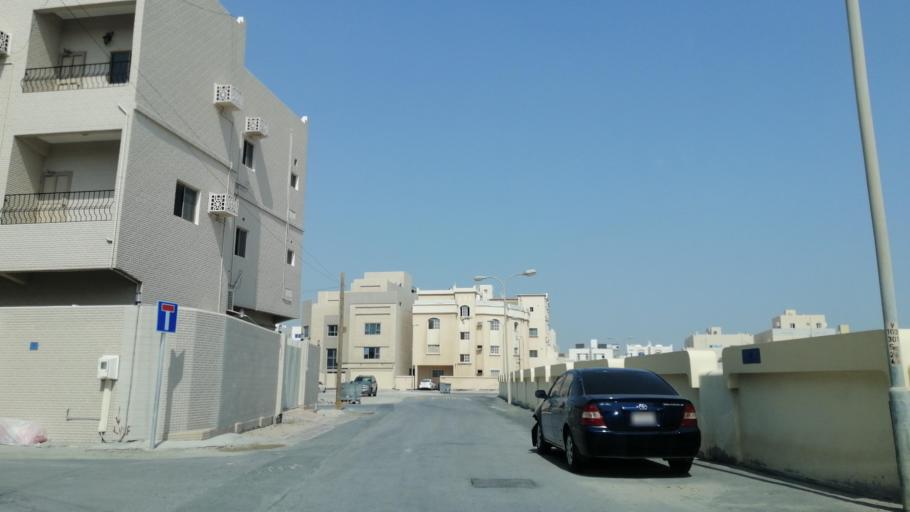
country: BH
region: Muharraq
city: Al Hadd
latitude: 26.2514
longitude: 50.6525
